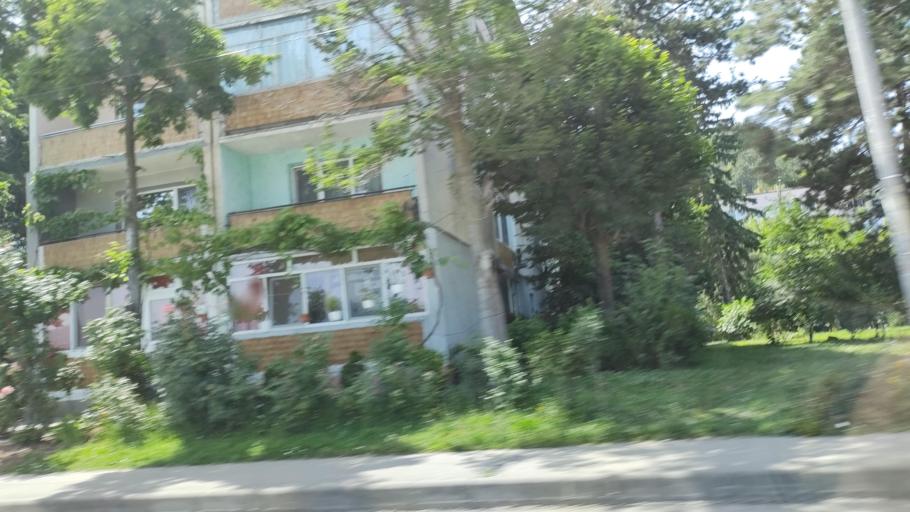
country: RO
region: Mehedinti
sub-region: Municipiul Orsova
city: Orsova
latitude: 44.7289
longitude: 22.4011
